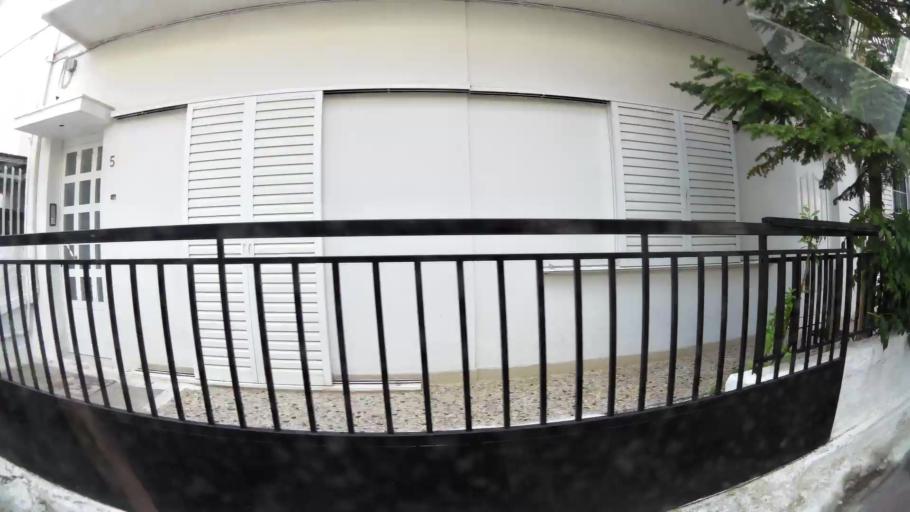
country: GR
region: Attica
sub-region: Nomarchia Dytikis Attikis
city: Zefyri
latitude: 38.0563
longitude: 23.7324
